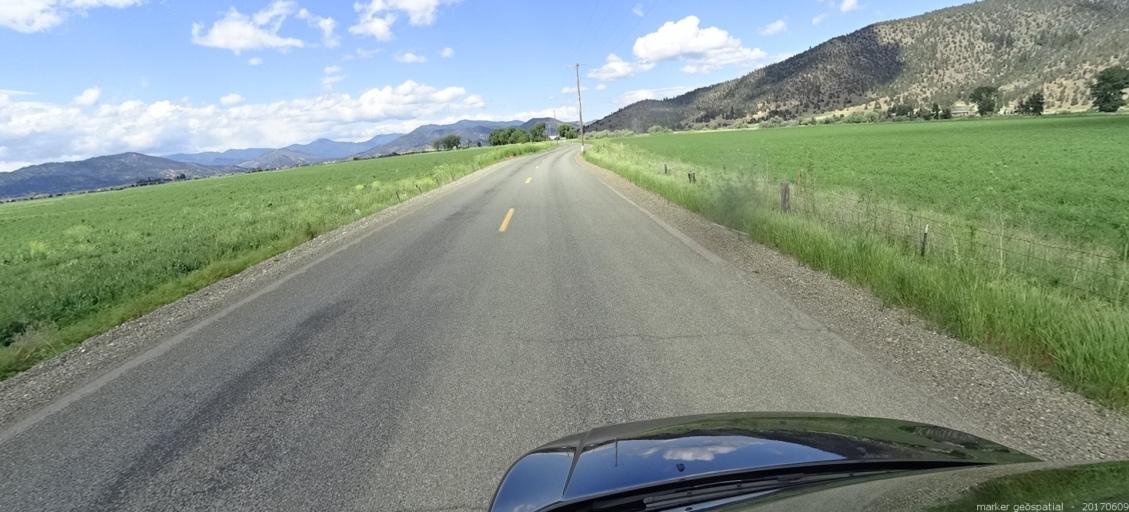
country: US
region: California
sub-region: Siskiyou County
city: Yreka
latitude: 41.5127
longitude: -122.8547
